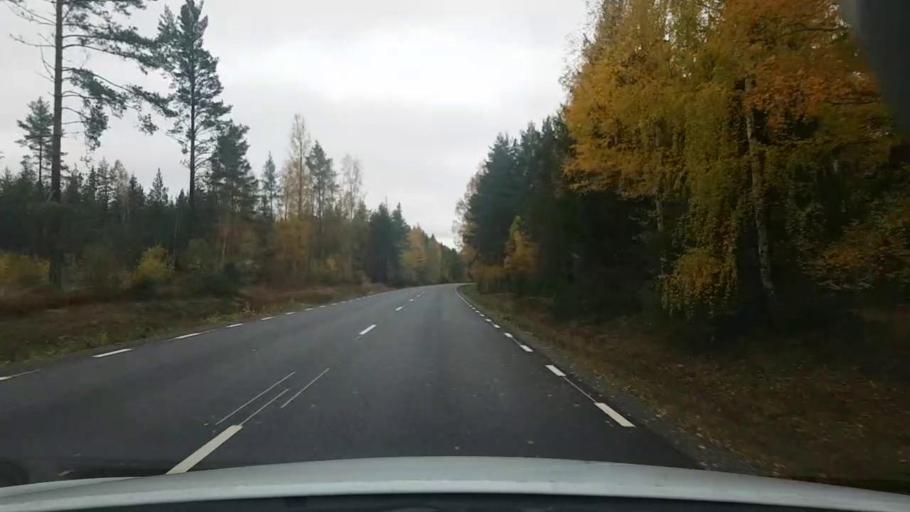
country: SE
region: OErebro
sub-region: Laxa Kommun
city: Laxa
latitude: 58.7916
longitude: 14.5412
